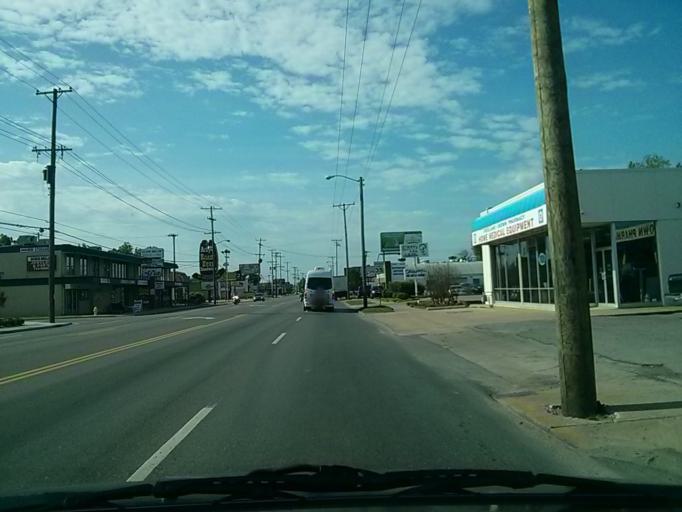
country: US
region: Oklahoma
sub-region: Tulsa County
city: Tulsa
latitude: 36.1039
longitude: -95.9758
